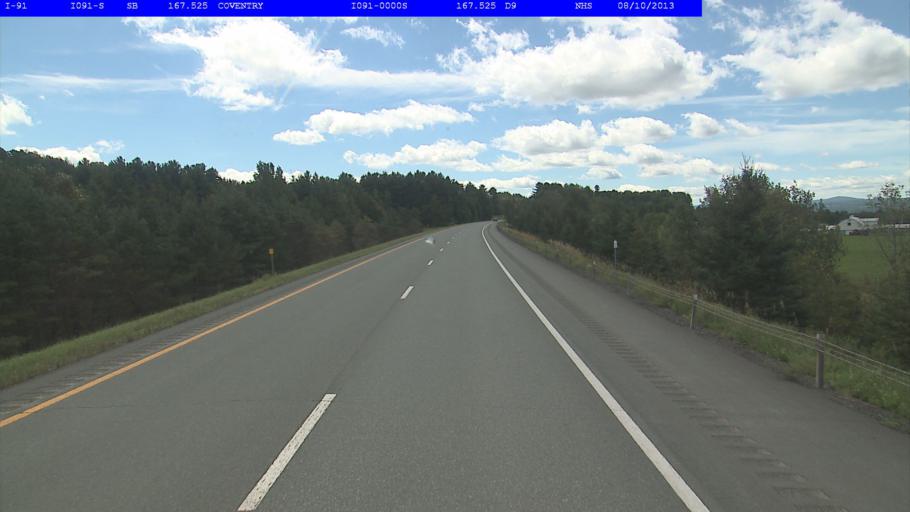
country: US
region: Vermont
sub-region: Orleans County
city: Newport
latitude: 44.8872
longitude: -72.1724
